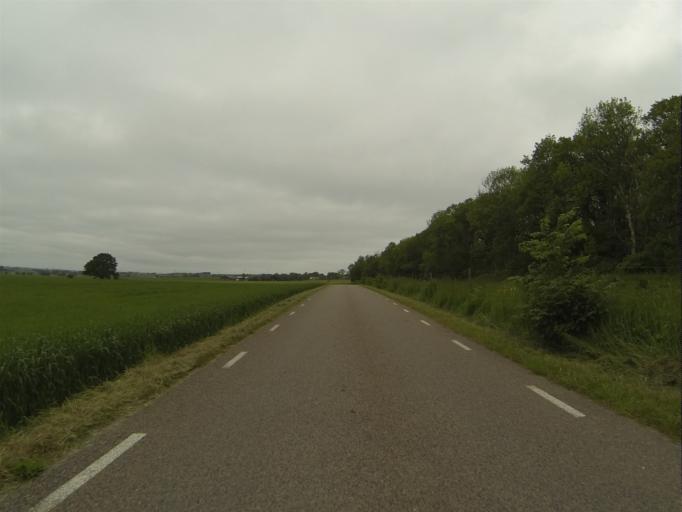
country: SE
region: Skane
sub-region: Lunds Kommun
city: Genarp
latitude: 55.6746
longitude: 13.3268
